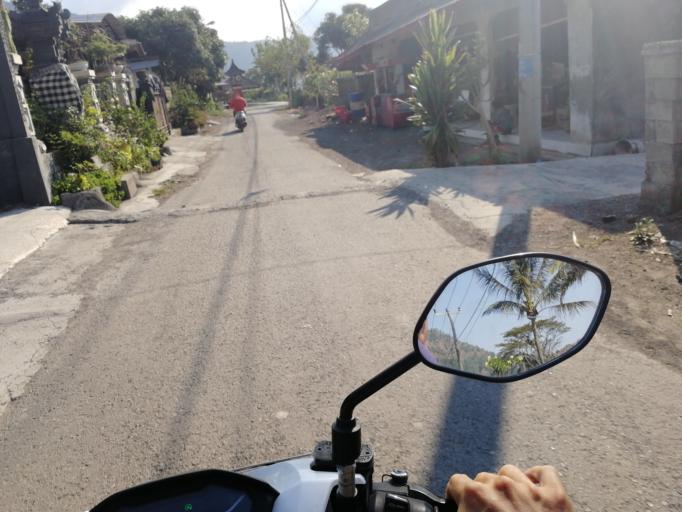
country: ID
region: Bali
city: Banjar Trunyan
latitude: -8.2713
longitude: 115.4155
